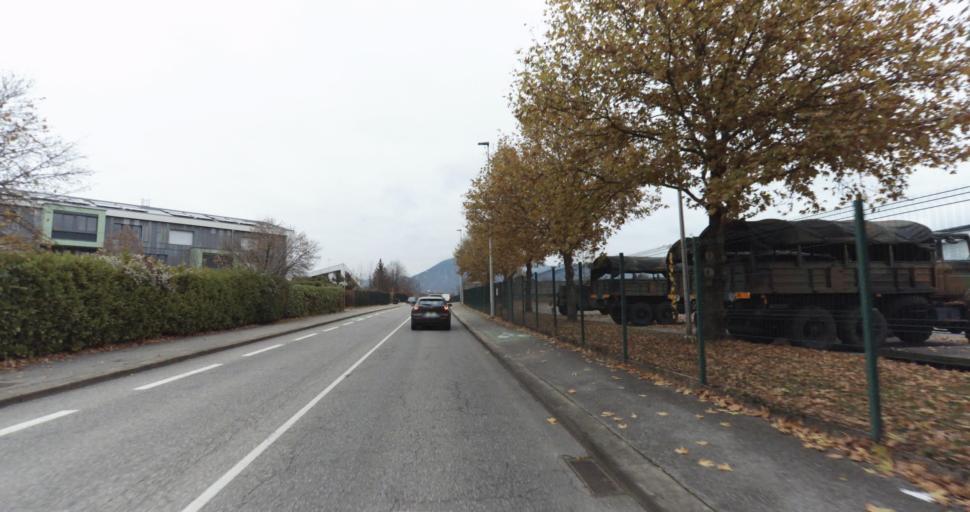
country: FR
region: Rhone-Alpes
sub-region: Departement de la Haute-Savoie
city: Cran-Gevrier
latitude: 45.8957
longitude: 6.0929
